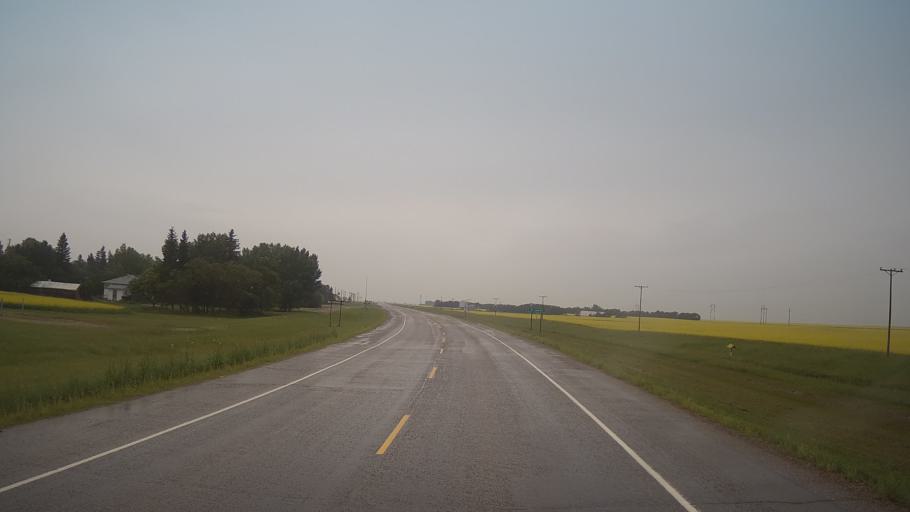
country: CA
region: Saskatchewan
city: Wilkie
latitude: 52.2018
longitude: -108.4449
